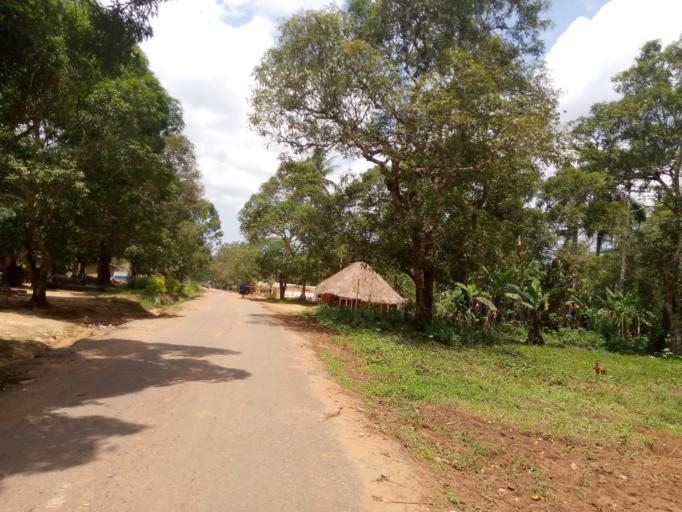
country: SL
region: Western Area
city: Waterloo
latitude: 8.3789
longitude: -12.9595
